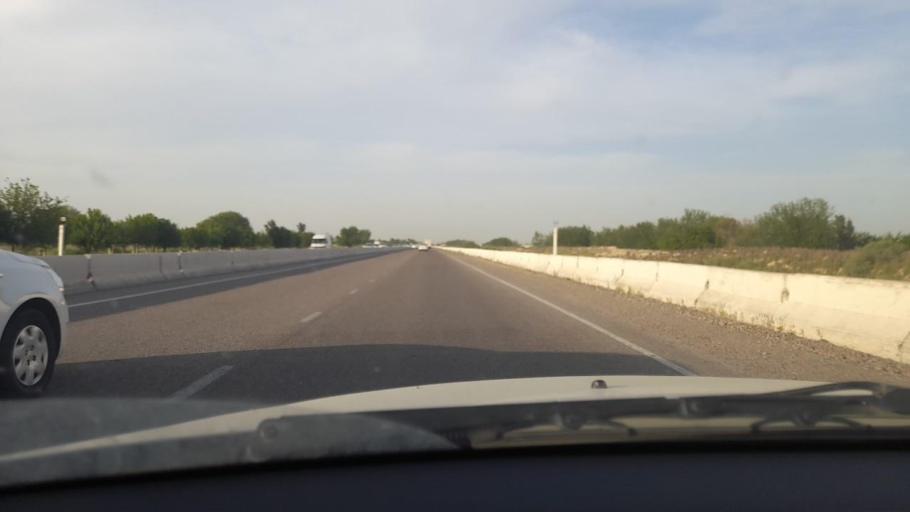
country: UZ
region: Jizzax
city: Gagarin
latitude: 40.4790
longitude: 68.2836
